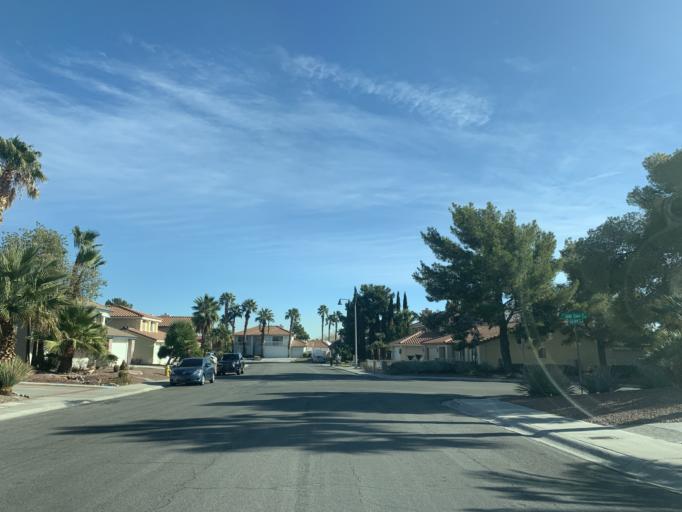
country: US
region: Nevada
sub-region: Clark County
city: Summerlin South
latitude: 36.1337
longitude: -115.2925
